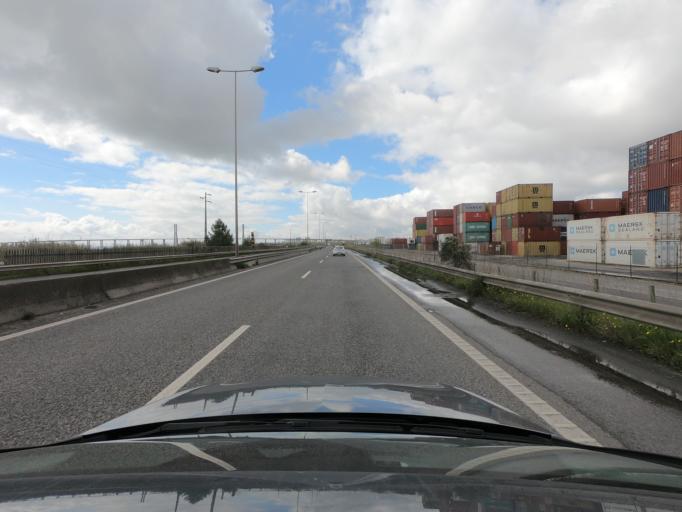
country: PT
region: Lisbon
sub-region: Loures
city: Bobadela
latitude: 38.8071
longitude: -9.0907
